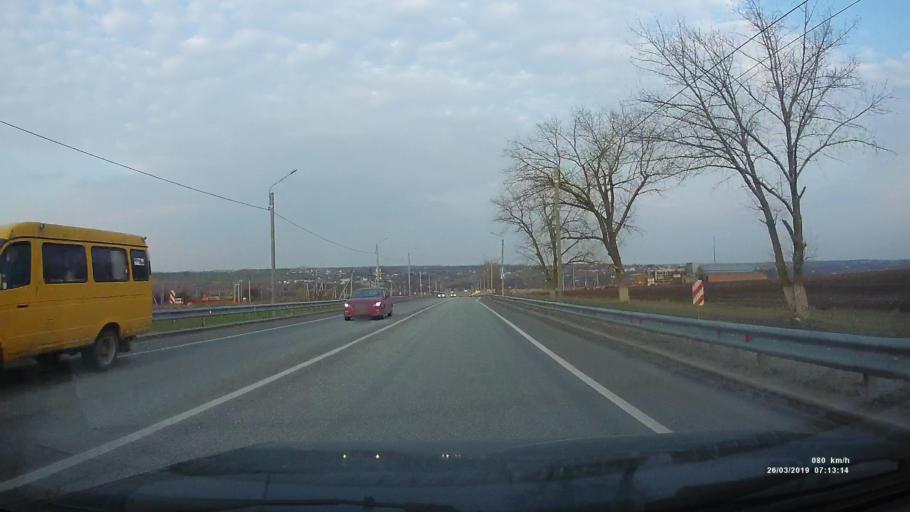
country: RU
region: Rostov
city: Primorka
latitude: 47.3211
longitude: 39.0390
